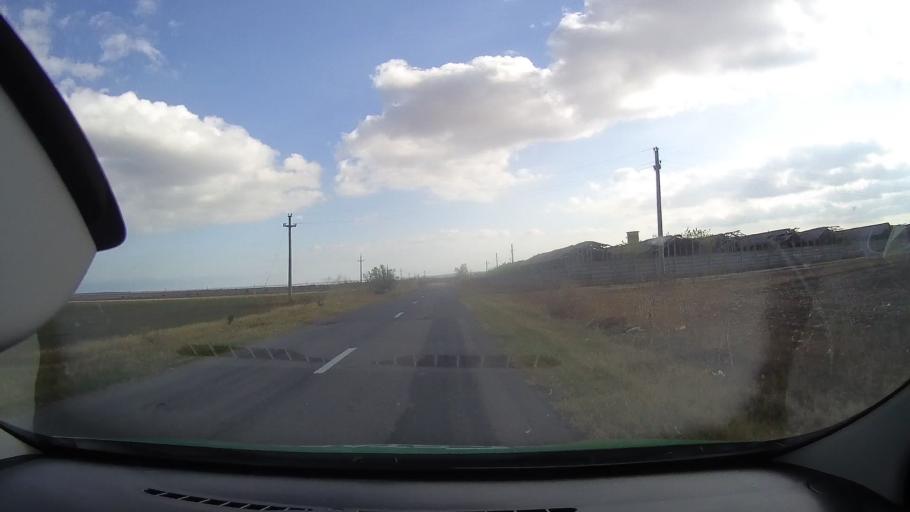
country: RO
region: Constanta
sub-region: Comuna Istria
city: Nuntasi
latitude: 44.5501
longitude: 28.6287
